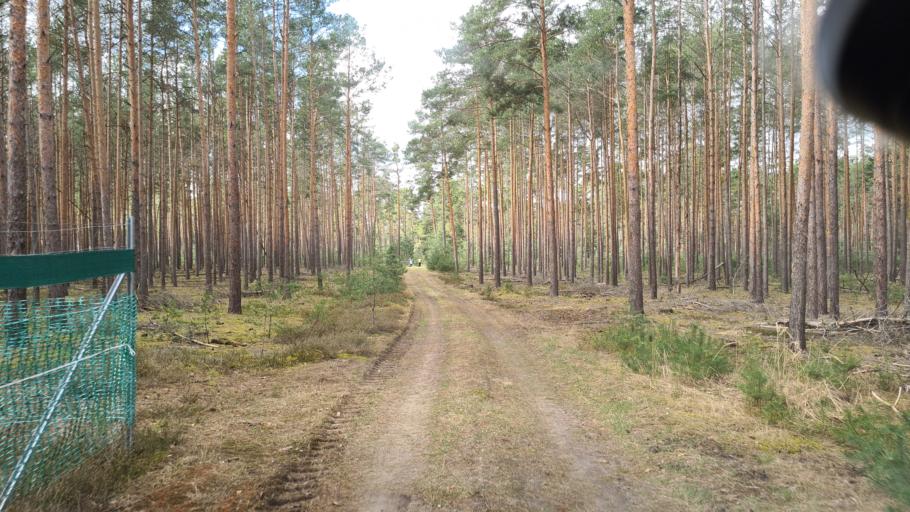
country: DE
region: Brandenburg
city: Trobitz
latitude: 51.6486
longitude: 13.4587
